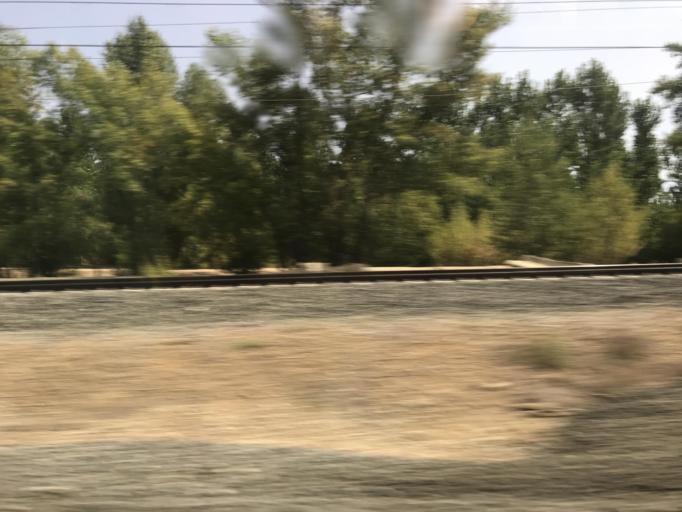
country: ES
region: Castille and Leon
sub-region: Provincia de Palencia
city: Soto de Cerrato
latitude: 41.9723
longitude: -4.4347
